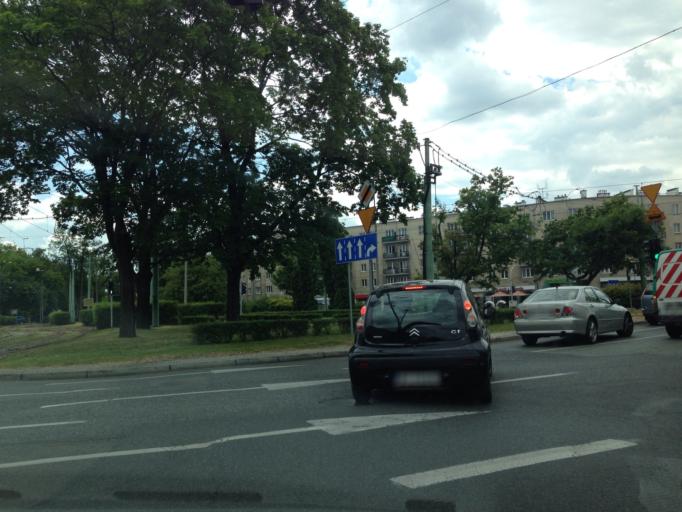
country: PL
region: Masovian Voivodeship
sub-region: Warszawa
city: Zoliborz
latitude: 52.2694
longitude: 20.9858
